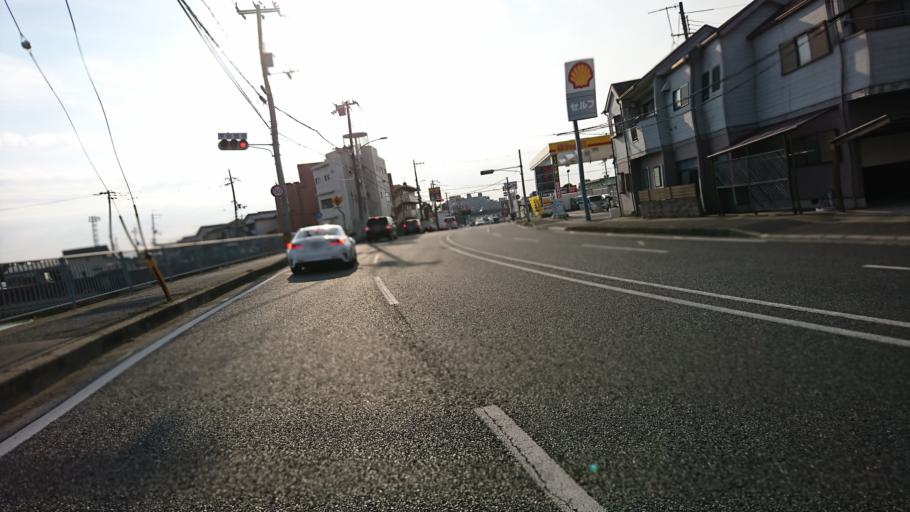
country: JP
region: Hyogo
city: Kakogawacho-honmachi
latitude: 34.7230
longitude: 134.8999
